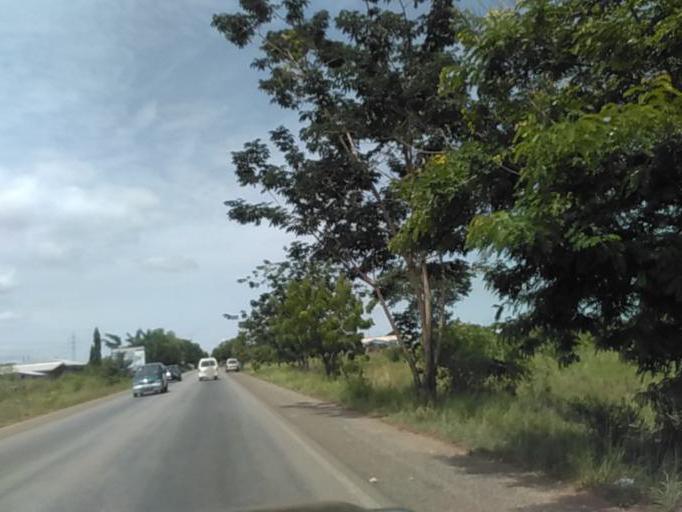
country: GH
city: Akropong
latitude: 6.1012
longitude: 0.0460
